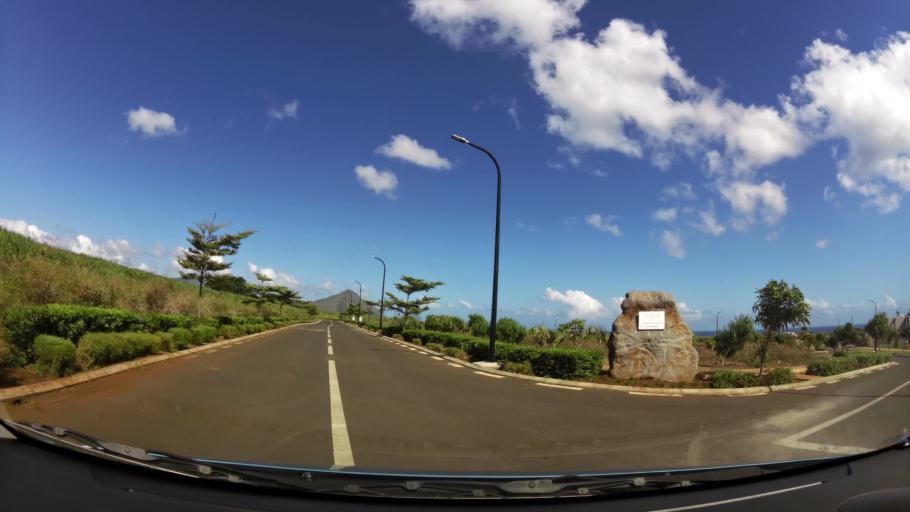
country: MU
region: Black River
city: Cascavelle
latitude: -20.2814
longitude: 57.3918
